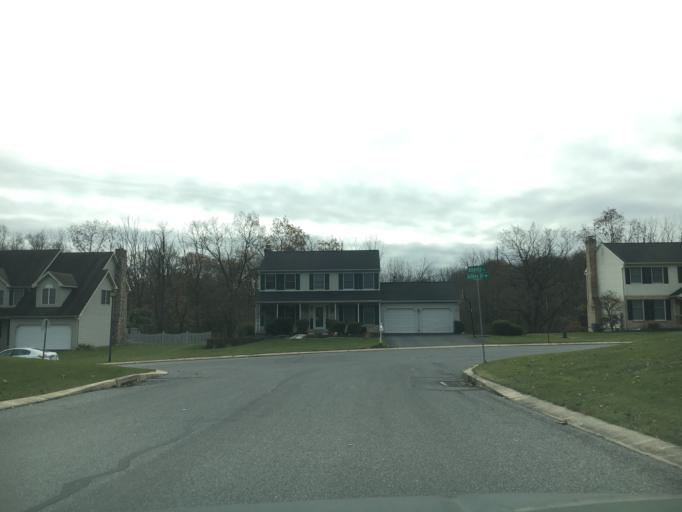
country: US
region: Pennsylvania
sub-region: Lehigh County
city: Laurys Station
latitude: 40.7213
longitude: -75.5333
